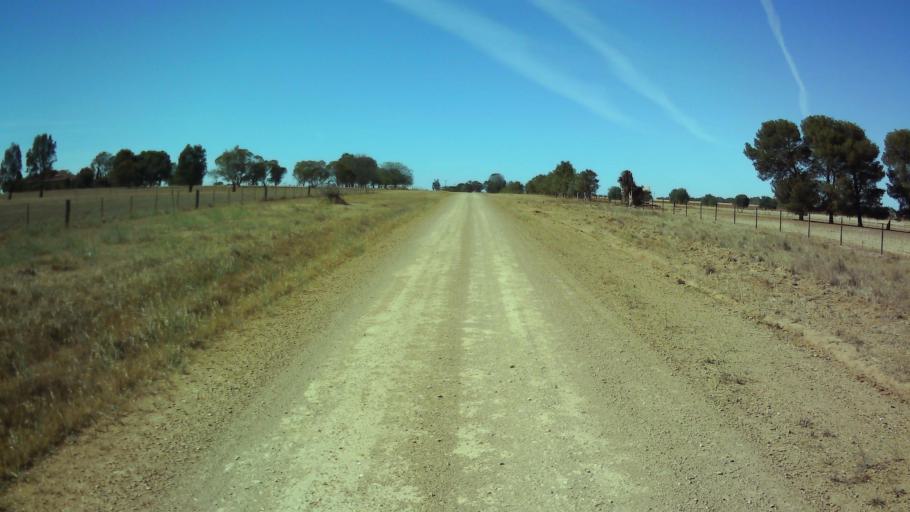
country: AU
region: New South Wales
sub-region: Weddin
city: Grenfell
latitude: -34.0539
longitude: 148.1722
